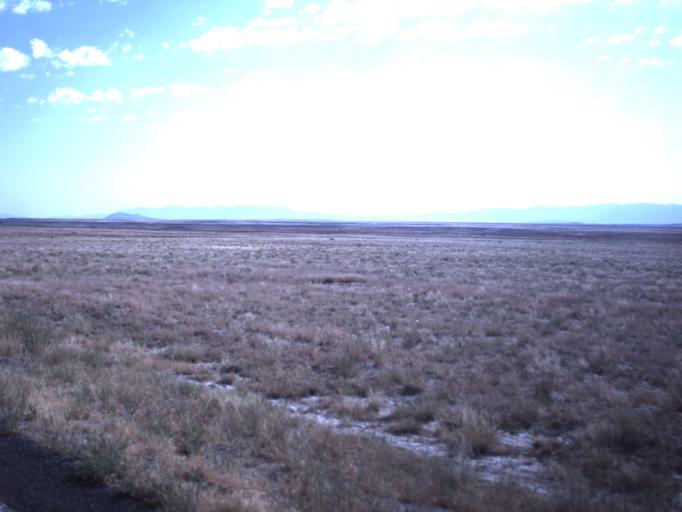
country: US
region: Utah
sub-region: Beaver County
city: Milford
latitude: 38.8525
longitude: -112.8416
